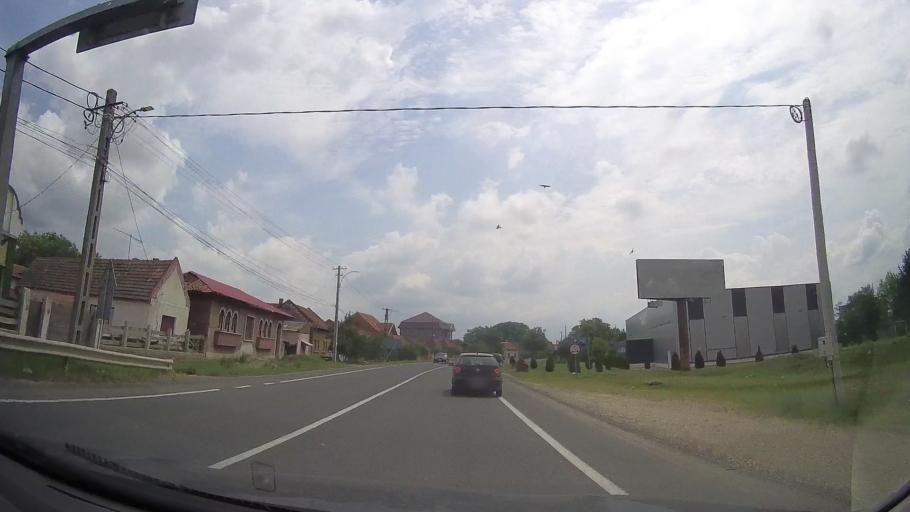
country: RO
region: Timis
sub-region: Comuna Costeiu
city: Costeiu
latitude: 45.7370
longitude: 21.8544
